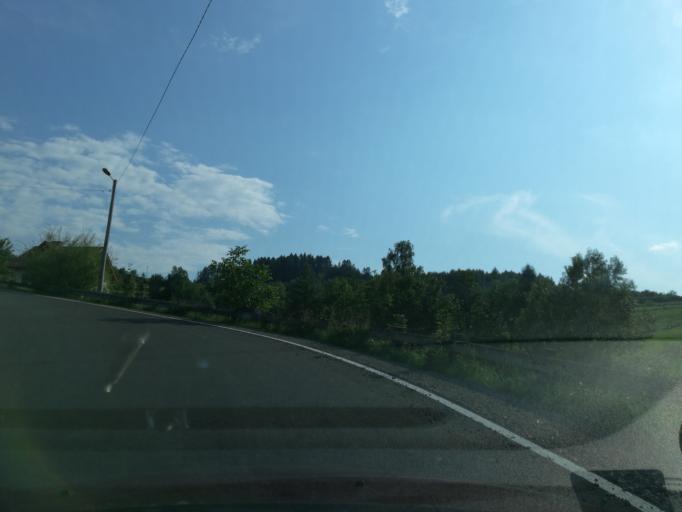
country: PL
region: Lesser Poland Voivodeship
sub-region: Powiat nowosadecki
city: Nawojowa
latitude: 49.5388
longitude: 20.7392
